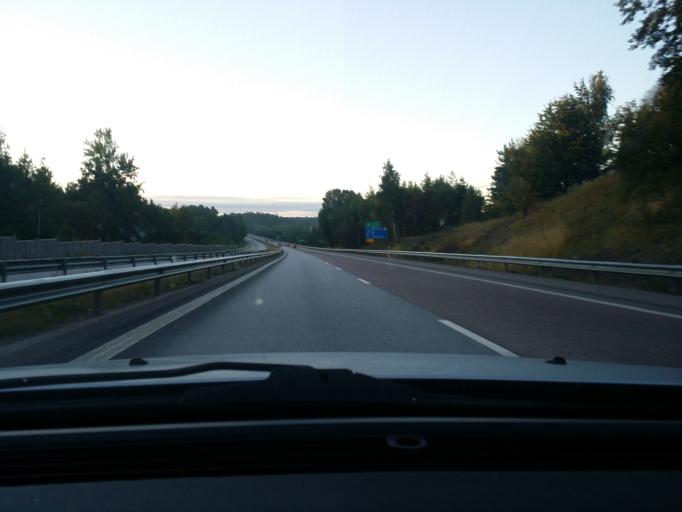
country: SE
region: Uppsala
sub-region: Habo Kommun
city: Balsta
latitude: 59.5744
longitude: 17.5438
